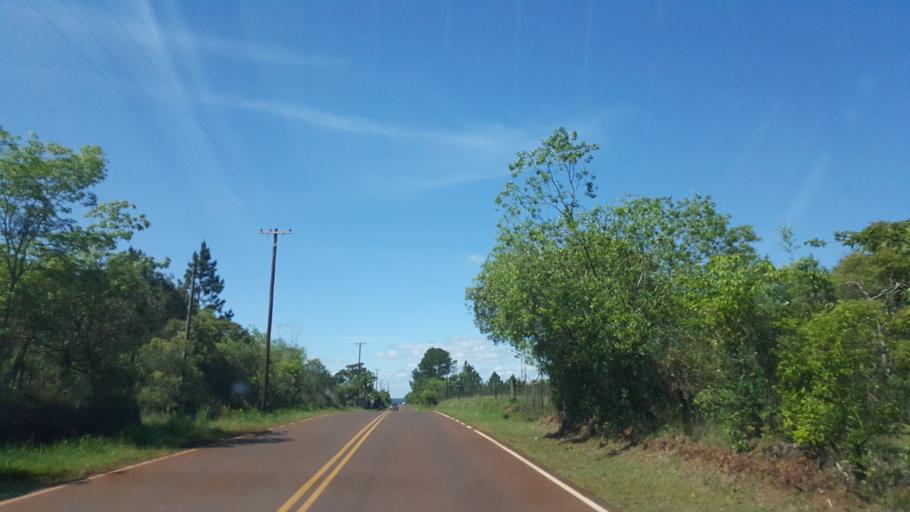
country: AR
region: Misiones
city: Garupa
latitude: -27.5027
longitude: -55.8508
